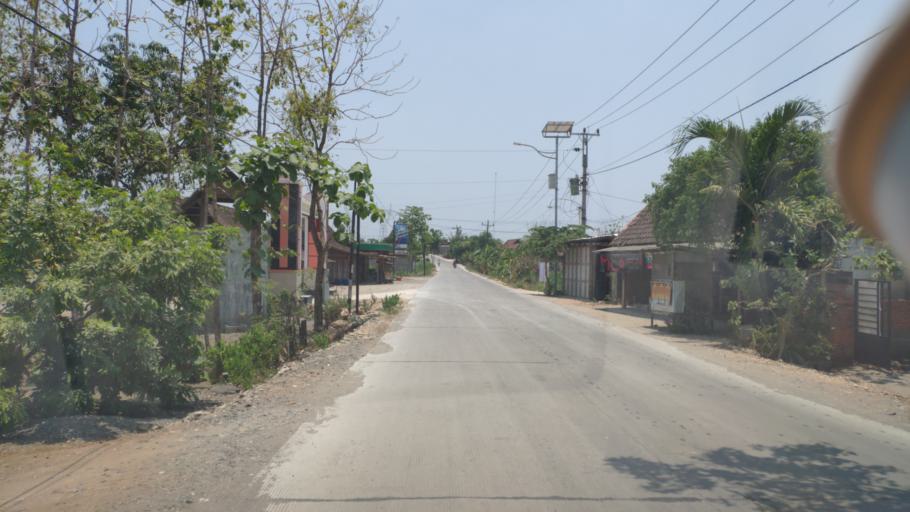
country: ID
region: Central Java
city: Temulus
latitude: -7.2300
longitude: 111.4148
